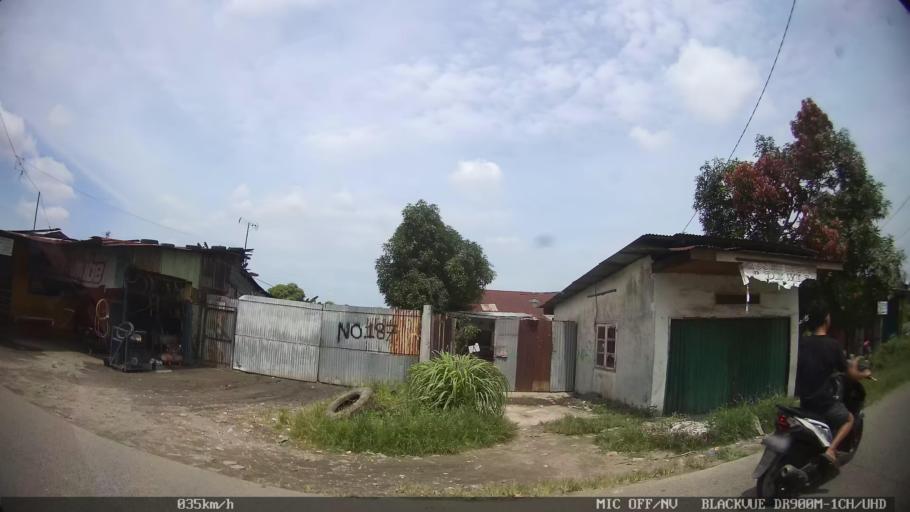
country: ID
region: North Sumatra
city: Medan
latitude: 3.6450
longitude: 98.6874
